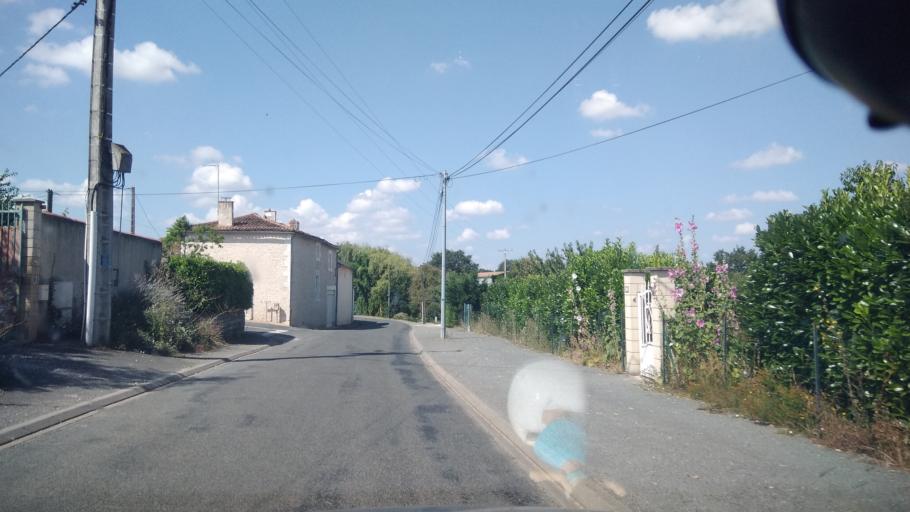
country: FR
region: Poitou-Charentes
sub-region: Departement de la Vienne
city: Ayron
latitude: 46.6521
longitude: 0.0666
